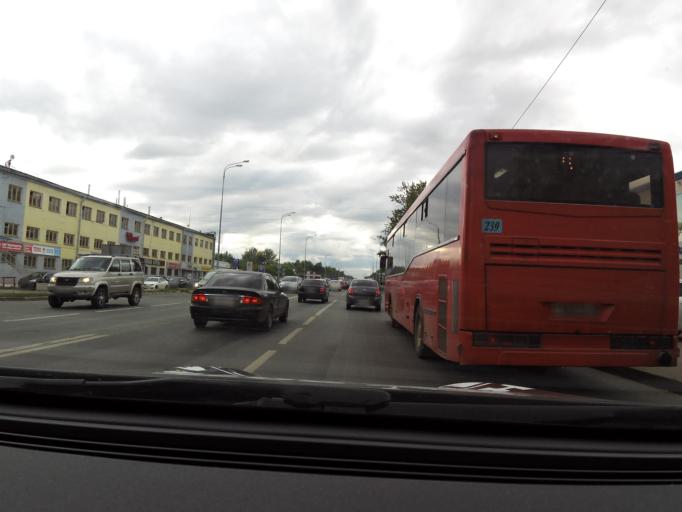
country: RU
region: Tatarstan
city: Staroye Arakchino
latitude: 55.8269
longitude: 49.0252
